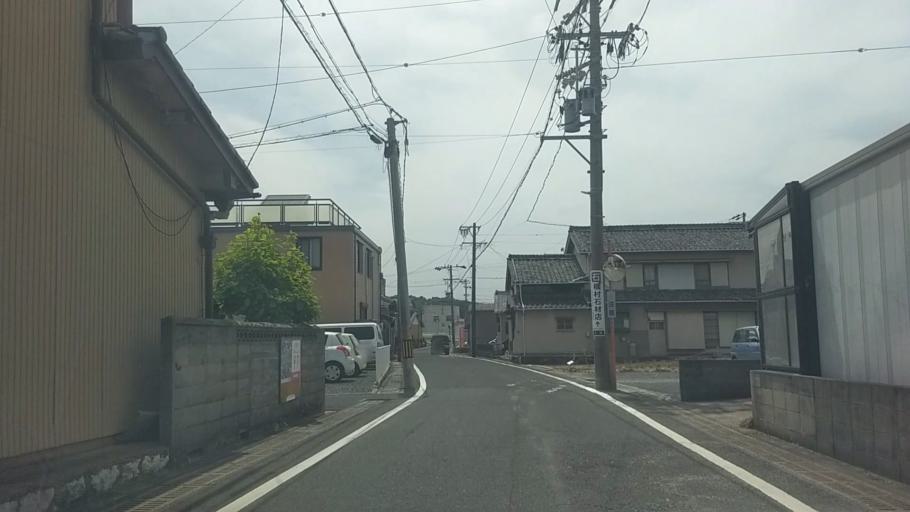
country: JP
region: Shizuoka
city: Kosai-shi
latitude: 34.7488
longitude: 137.5290
